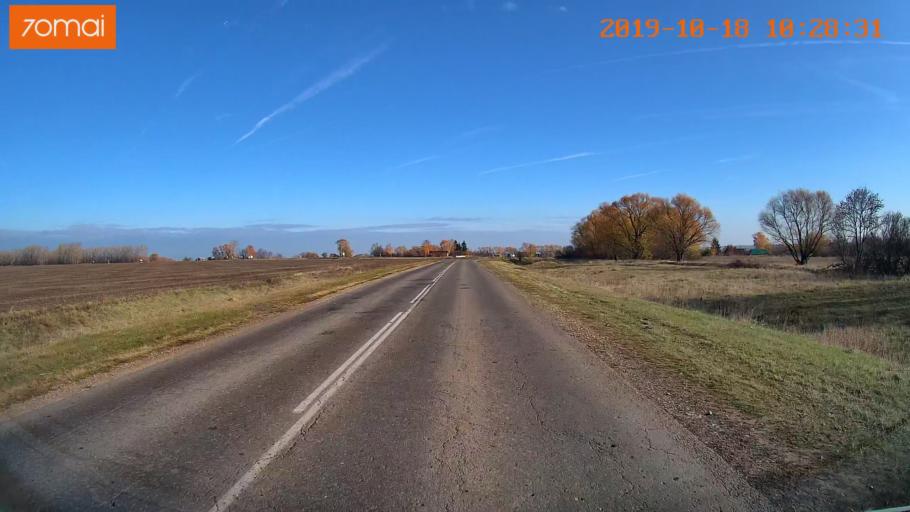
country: RU
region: Tula
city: Kurkino
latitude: 53.4450
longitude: 38.6567
